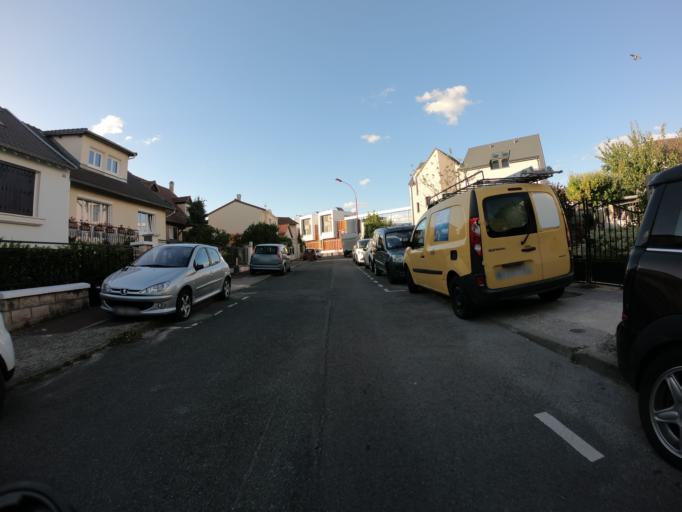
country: FR
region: Ile-de-France
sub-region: Departement du Val-de-Marne
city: Fresnes
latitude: 48.7570
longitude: 2.3206
